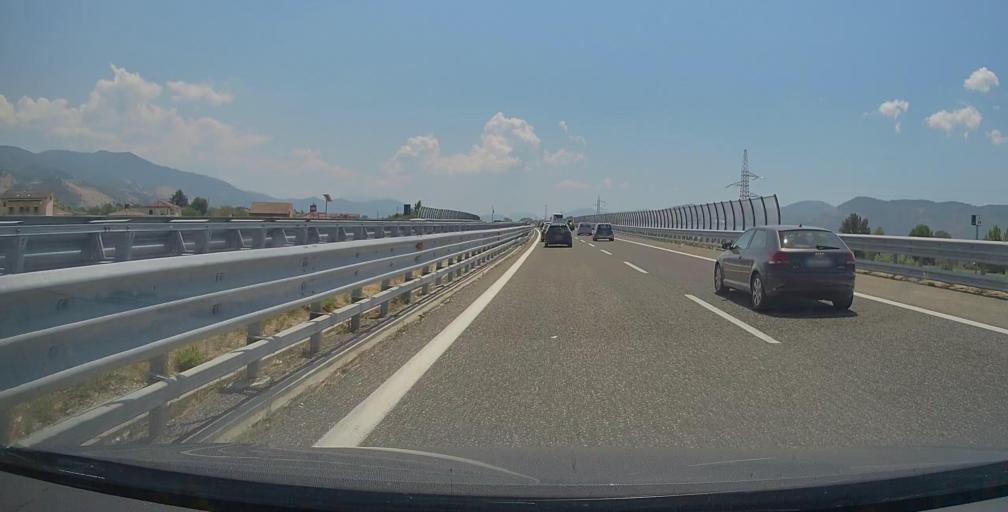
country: IT
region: Campania
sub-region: Provincia di Salerno
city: Sala Consilina
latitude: 40.3703
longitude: 15.6007
